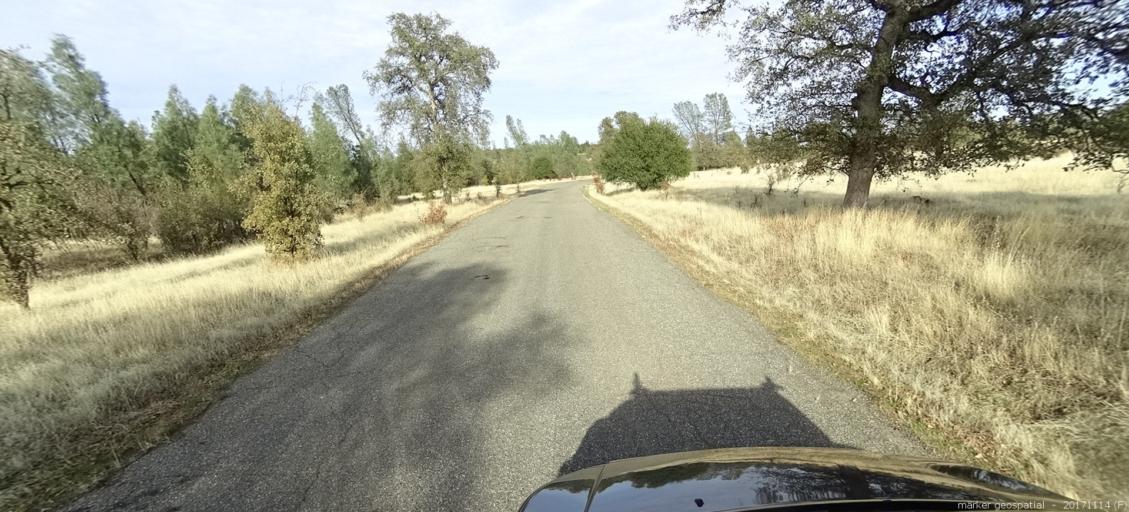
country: US
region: California
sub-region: Shasta County
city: Shasta
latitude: 40.3945
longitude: -122.5325
